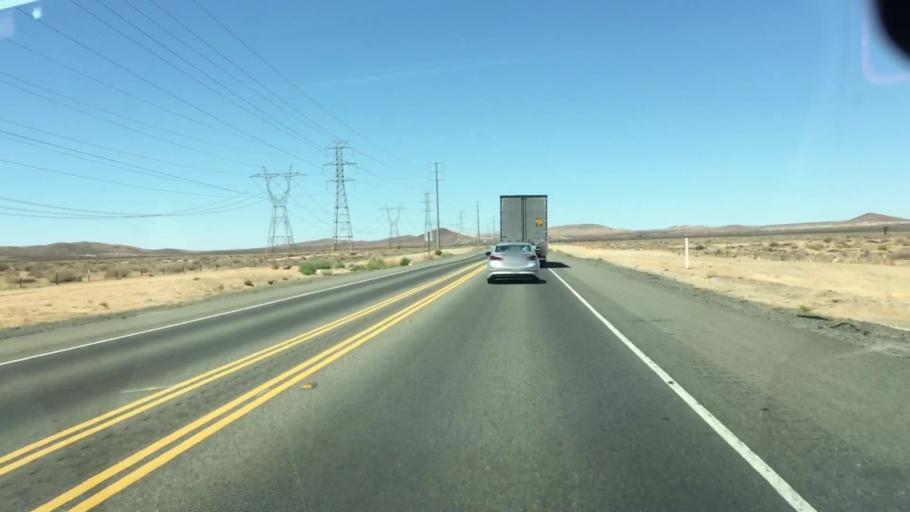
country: US
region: California
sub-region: Kern County
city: Boron
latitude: 34.8217
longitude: -117.4943
